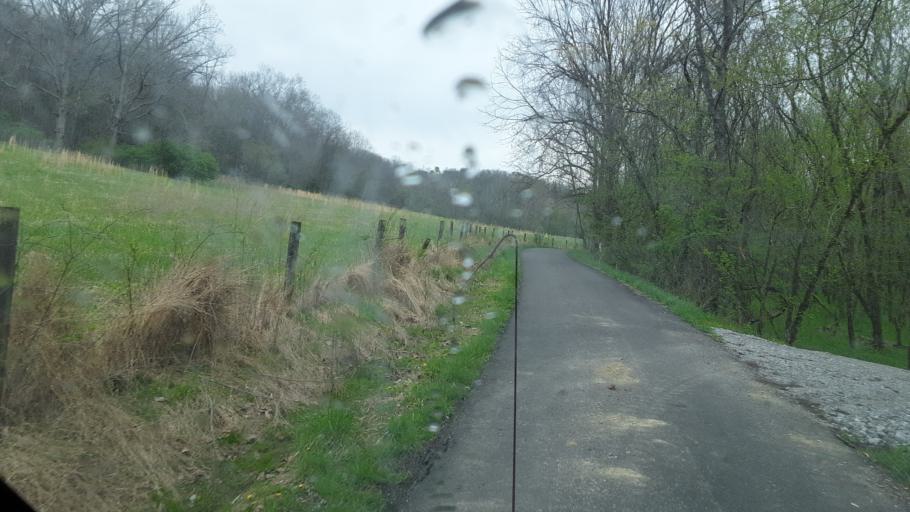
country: US
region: Kentucky
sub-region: Owen County
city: Owenton
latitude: 38.6713
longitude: -84.7941
